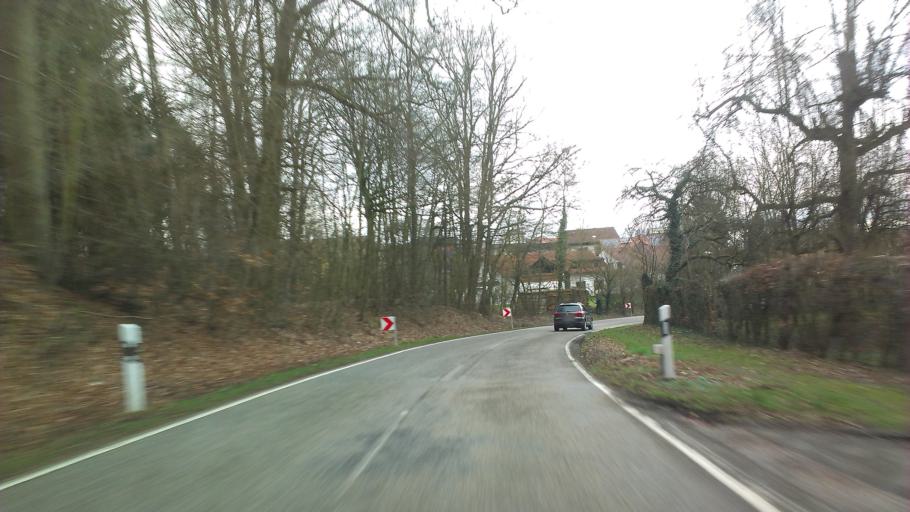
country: DE
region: Baden-Wuerttemberg
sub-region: Karlsruhe Region
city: Sulzfeld
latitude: 49.0927
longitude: 8.8976
